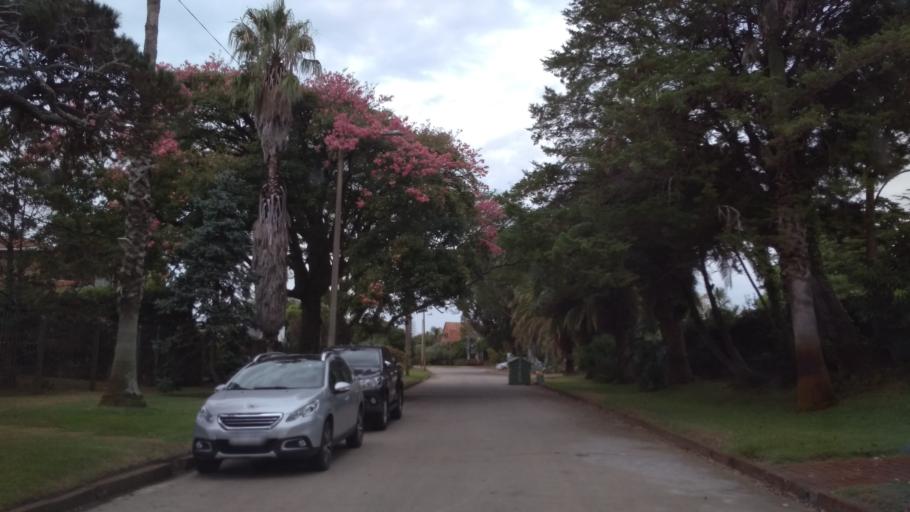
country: UY
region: Canelones
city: Barra de Carrasco
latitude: -34.8863
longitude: -56.0492
